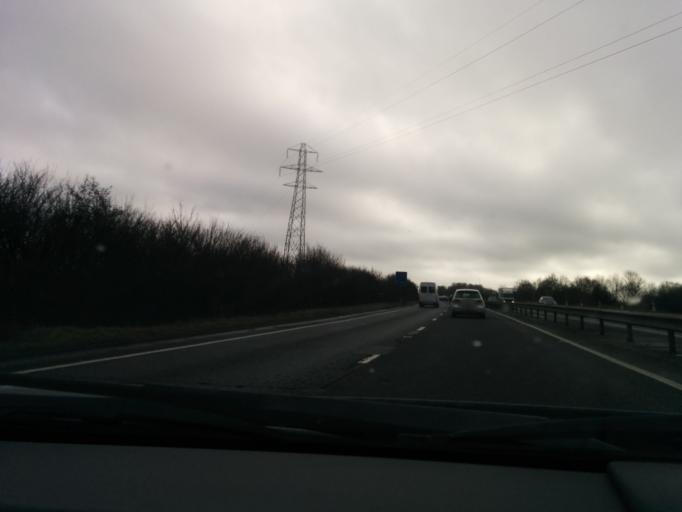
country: GB
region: England
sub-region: Oxfordshire
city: Marcham
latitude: 51.6412
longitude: -1.3189
